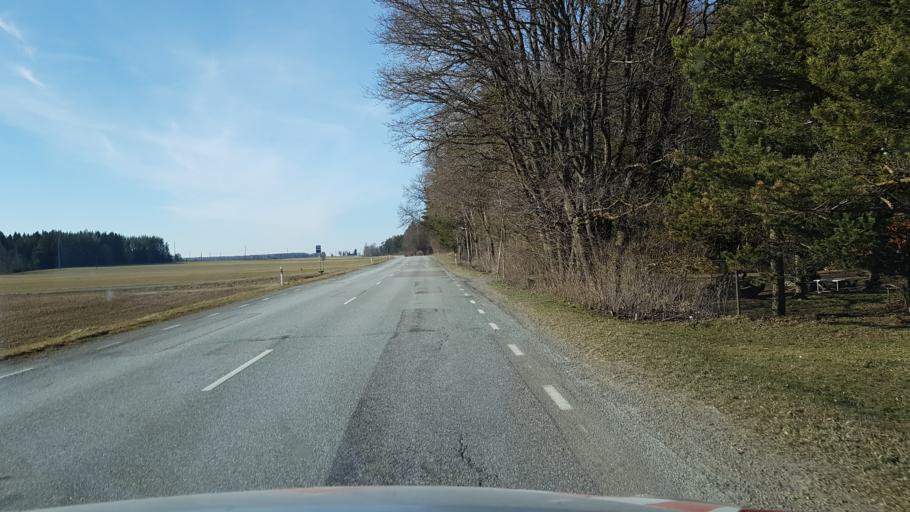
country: EE
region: Laeaene-Virumaa
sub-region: Vinni vald
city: Vinni
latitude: 59.1874
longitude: 26.5749
